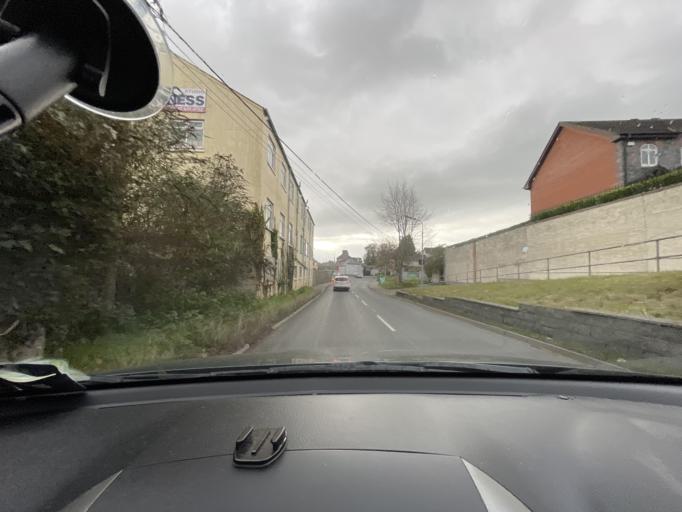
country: IE
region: Leinster
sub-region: Lu
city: Drogheda
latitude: 53.7195
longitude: -6.3297
